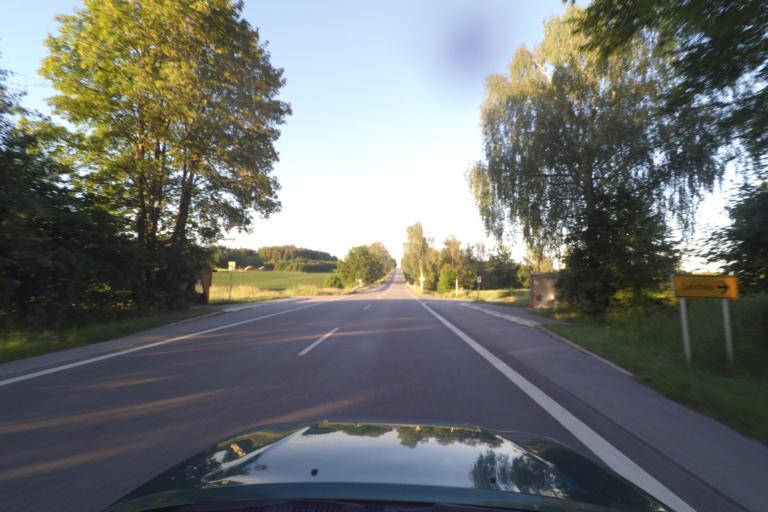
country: DE
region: Bavaria
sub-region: Upper Palatinate
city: Puchersreuth
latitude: 49.8217
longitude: 12.2696
